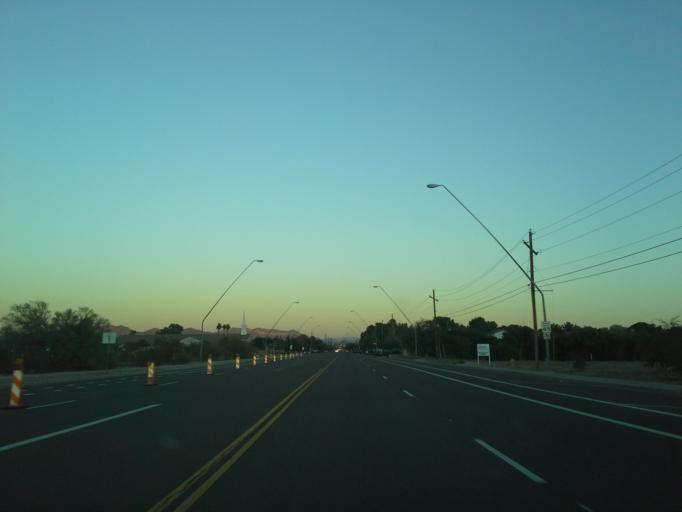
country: US
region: Arizona
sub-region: Maricopa County
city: Mesa
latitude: 33.4664
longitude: -111.7616
